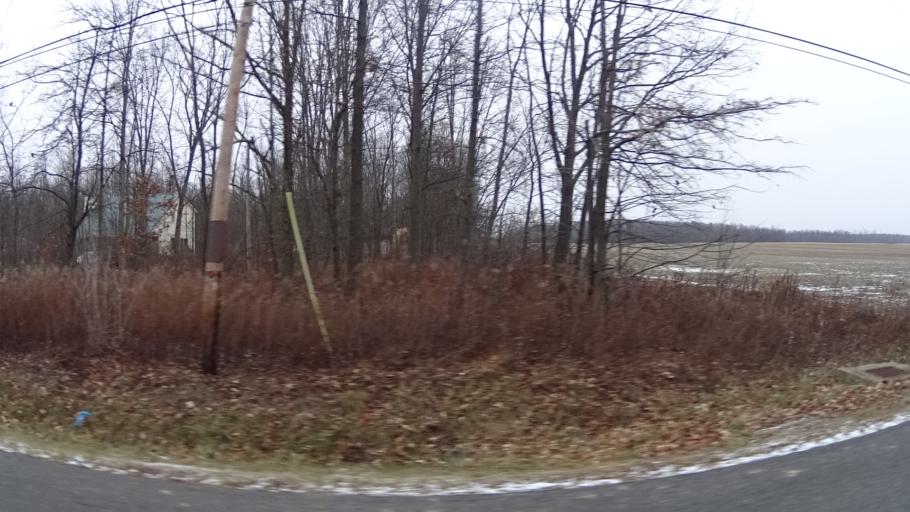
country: US
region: Ohio
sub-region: Lorain County
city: Lagrange
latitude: 41.2222
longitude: -82.1098
